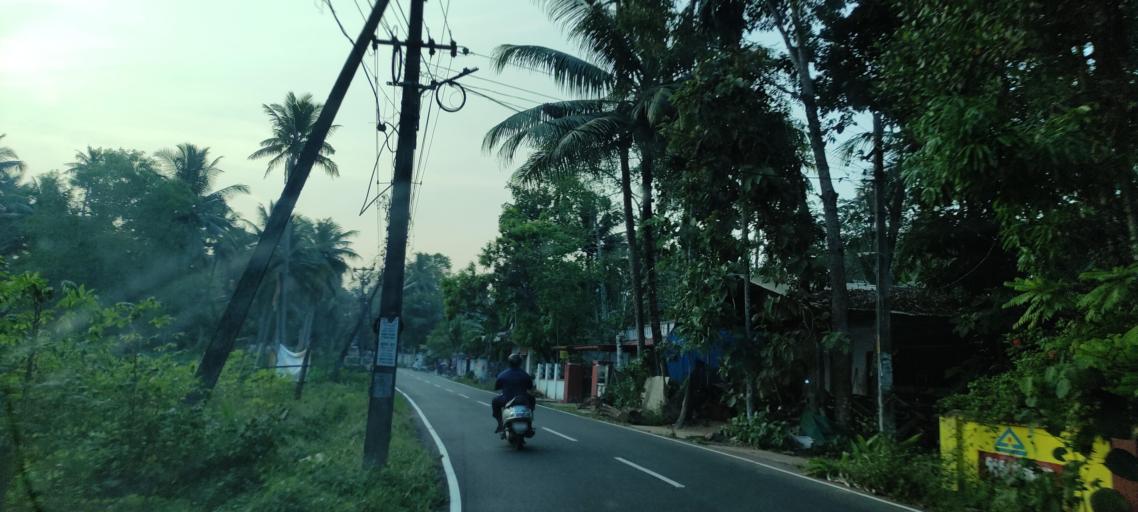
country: IN
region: Kerala
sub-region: Alappuzha
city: Mavelikara
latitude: 9.2681
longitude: 76.5432
